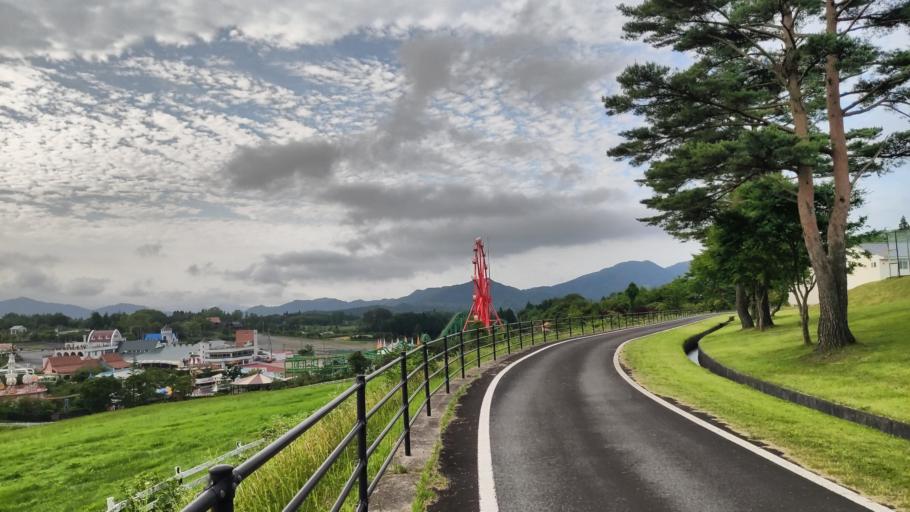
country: JP
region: Tottori
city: Kurayoshi
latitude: 35.2933
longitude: 133.6322
